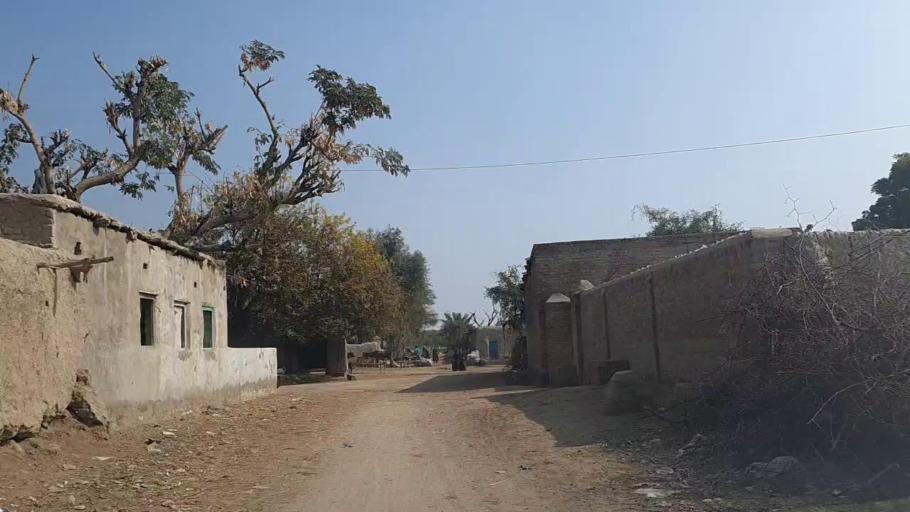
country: PK
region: Sindh
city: Daur
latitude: 26.3887
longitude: 68.4441
